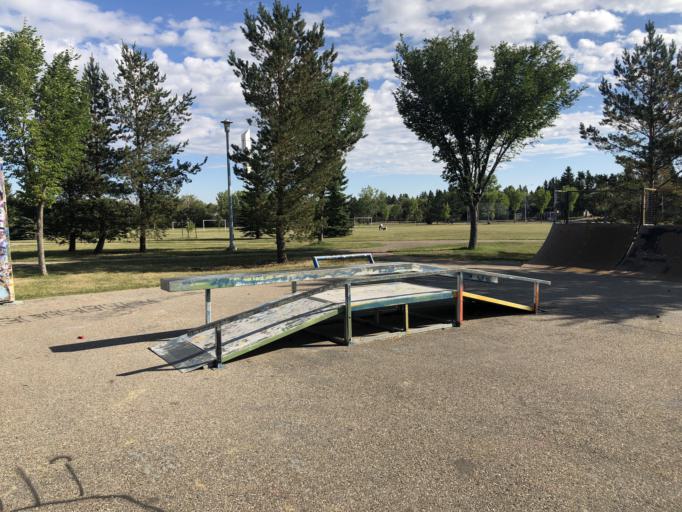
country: CA
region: Alberta
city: Edmonton
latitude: 53.4815
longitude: -113.5817
